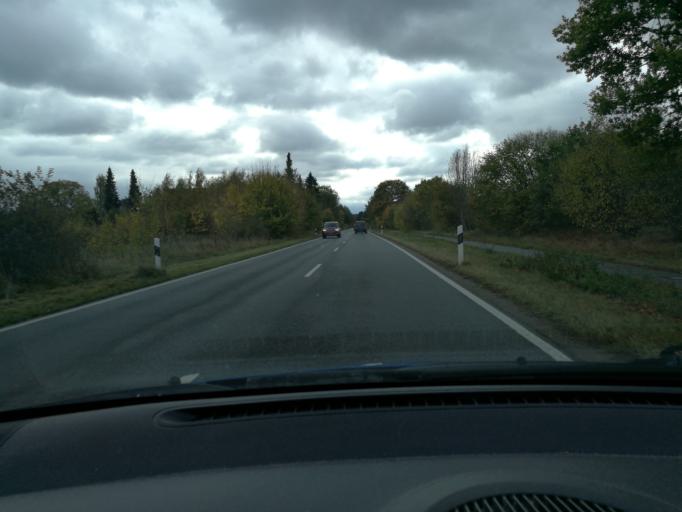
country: DE
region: Schleswig-Holstein
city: Gross Sarau
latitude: 53.7663
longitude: 10.7332
